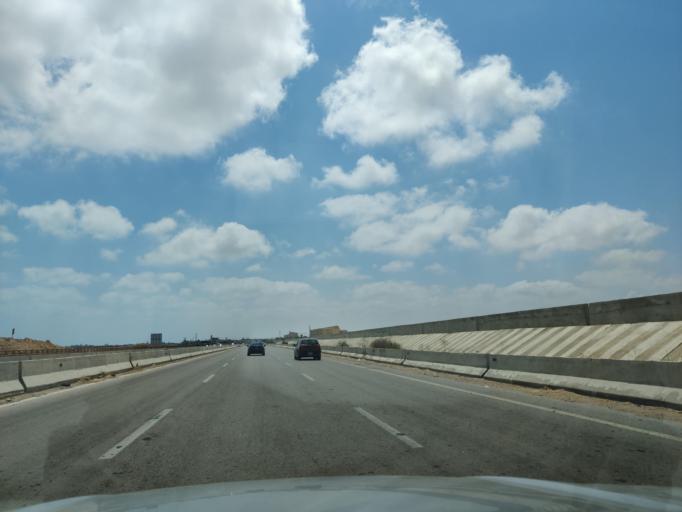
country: EG
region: Muhafazat Matruh
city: Al `Alamayn
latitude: 30.8214
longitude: 29.0069
